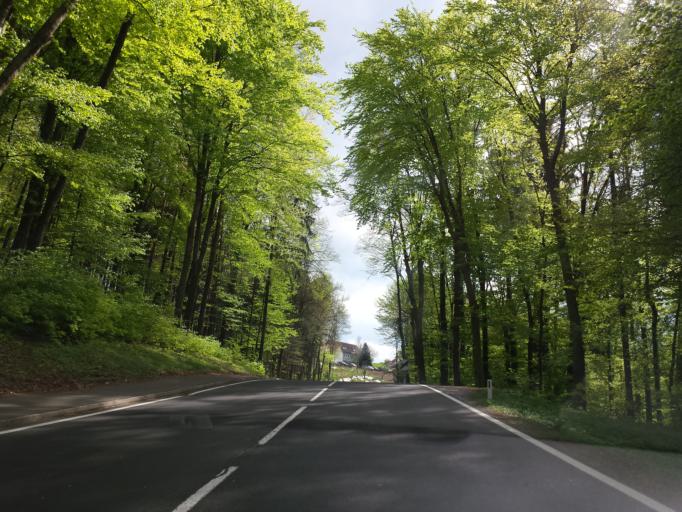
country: AT
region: Styria
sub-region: Politischer Bezirk Suedoststeiermark
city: Riegersburg
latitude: 46.9933
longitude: 15.9278
